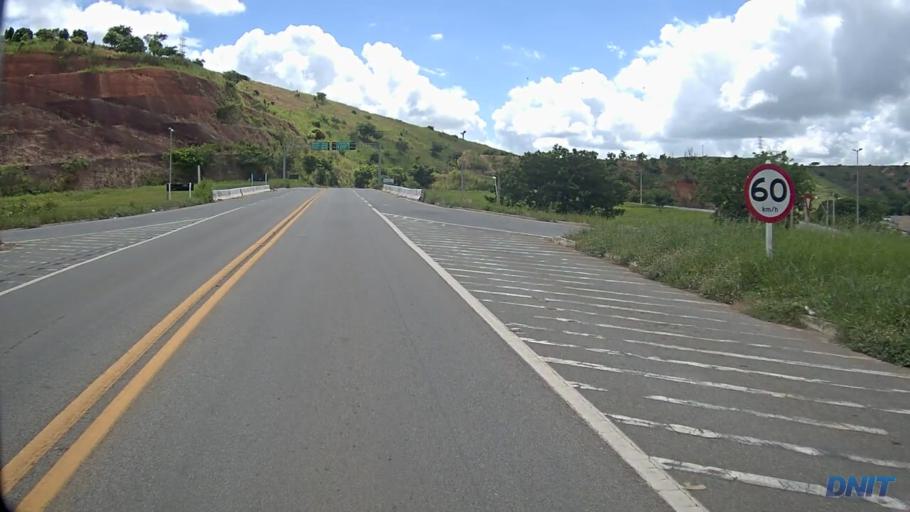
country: BR
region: Minas Gerais
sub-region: Governador Valadares
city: Governador Valadares
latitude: -18.8582
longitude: -41.9847
